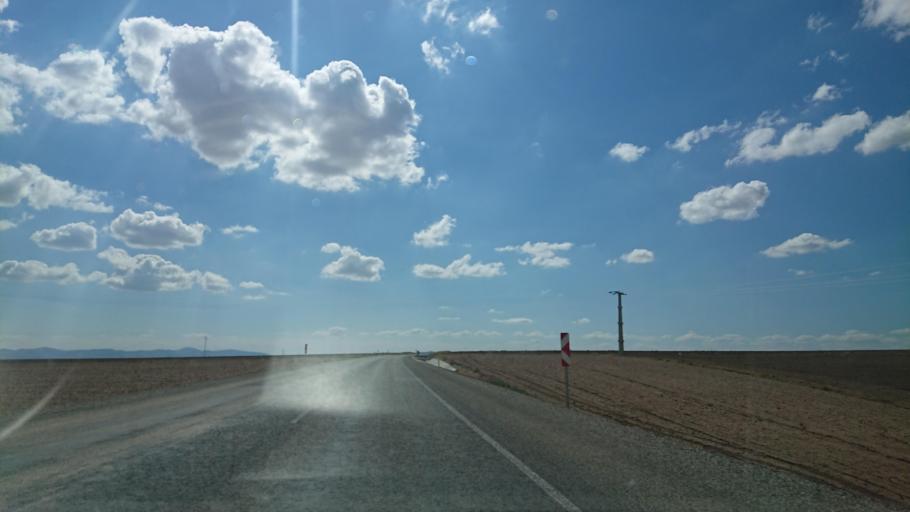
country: TR
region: Kirsehir
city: Kirsehir
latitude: 39.1219
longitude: 34.0101
